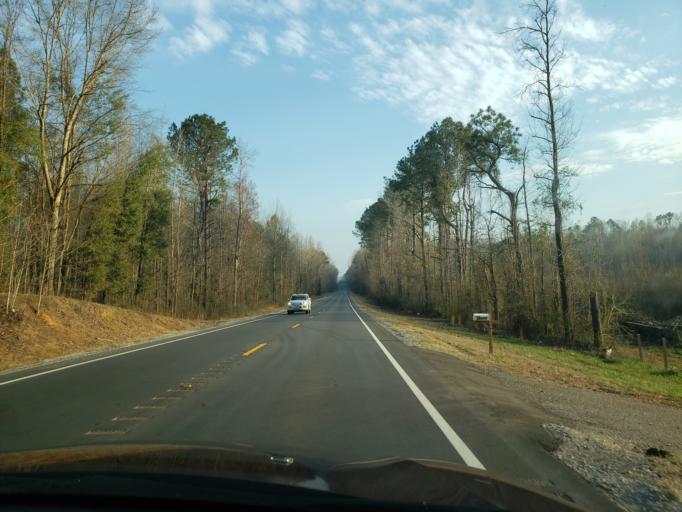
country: US
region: Alabama
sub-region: Hale County
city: Greensboro
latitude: 32.8485
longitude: -87.6111
